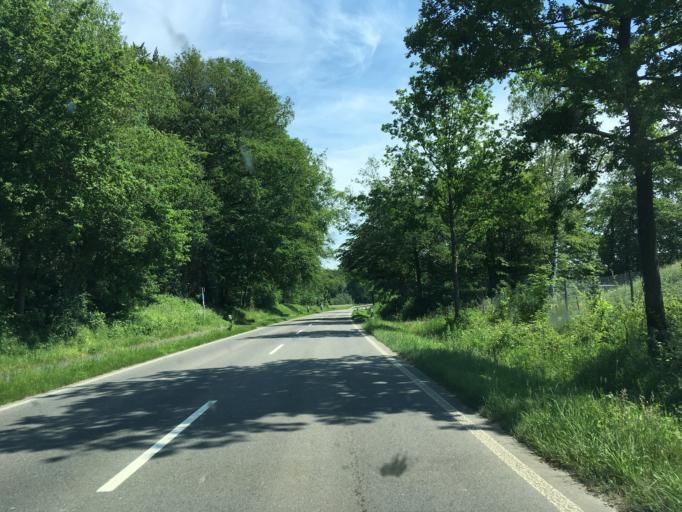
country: DE
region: North Rhine-Westphalia
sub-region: Regierungsbezirk Munster
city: Borken
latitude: 51.8347
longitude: 6.7838
